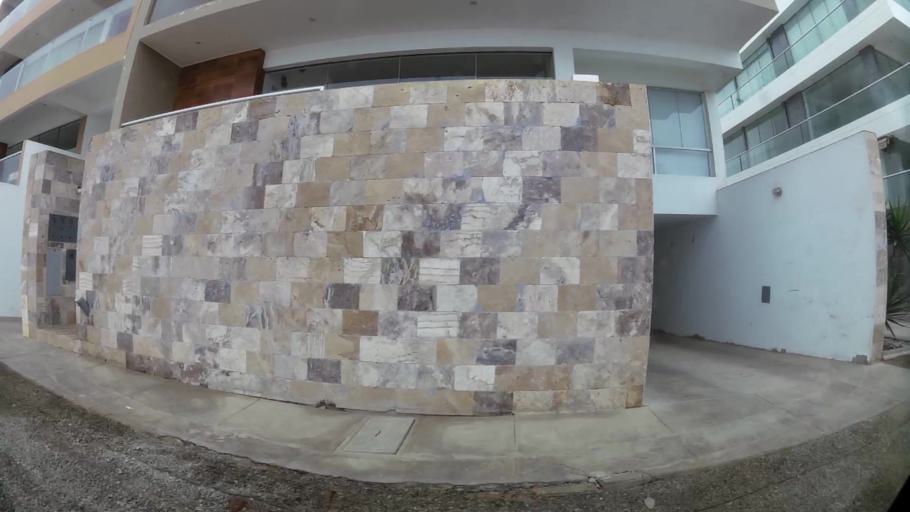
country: PE
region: Lima
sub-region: Lima
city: Punta Hermosa
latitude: -12.3269
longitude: -76.8337
